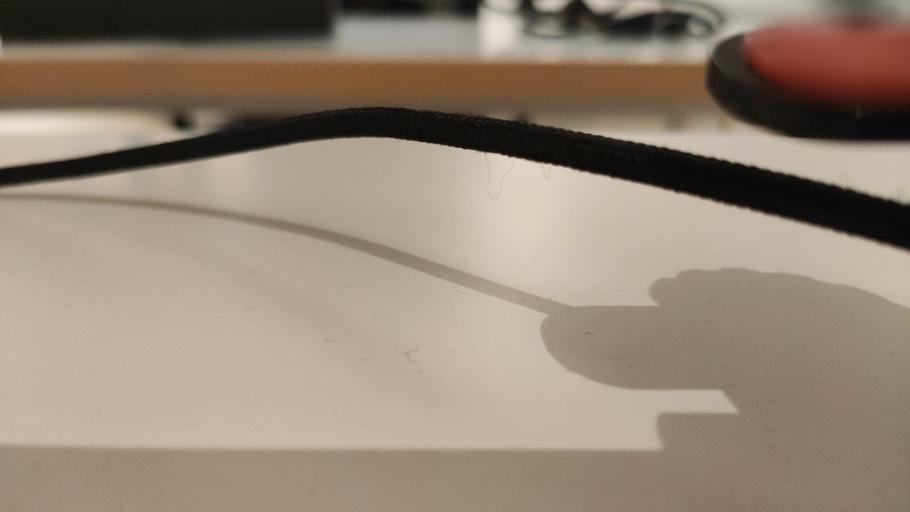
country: RU
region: Moskovskaya
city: Dorokhovo
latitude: 55.5283
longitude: 36.3571
